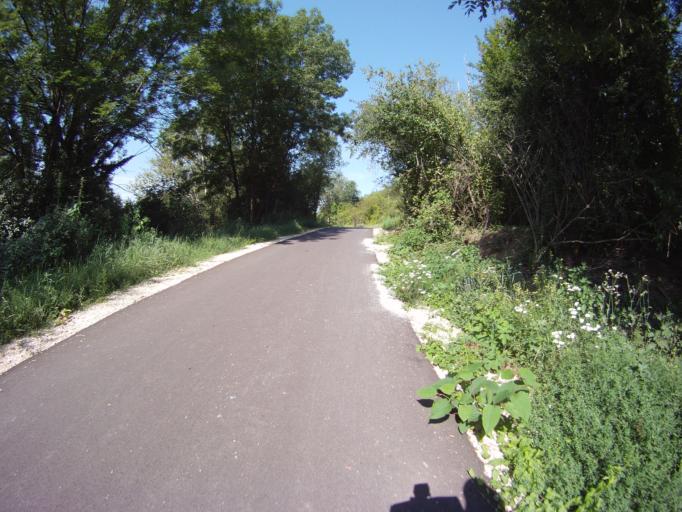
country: FR
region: Lorraine
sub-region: Departement de Meurthe-et-Moselle
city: Liverdun
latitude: 48.7581
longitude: 6.0507
